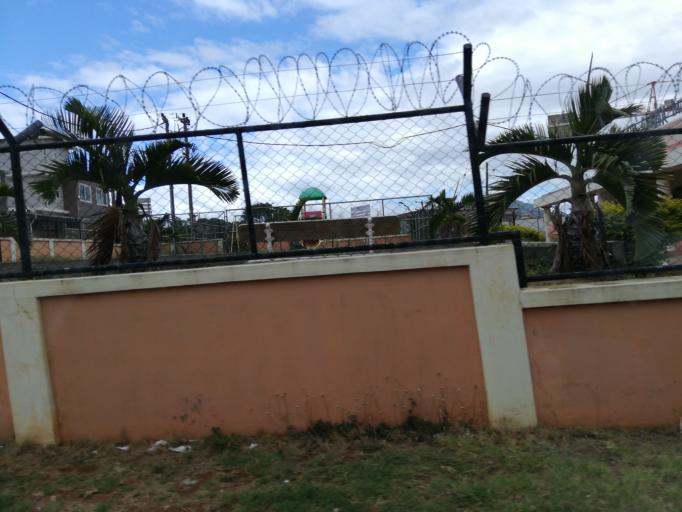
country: MU
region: Black River
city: Petite Riviere
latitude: -20.2118
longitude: 57.4641
